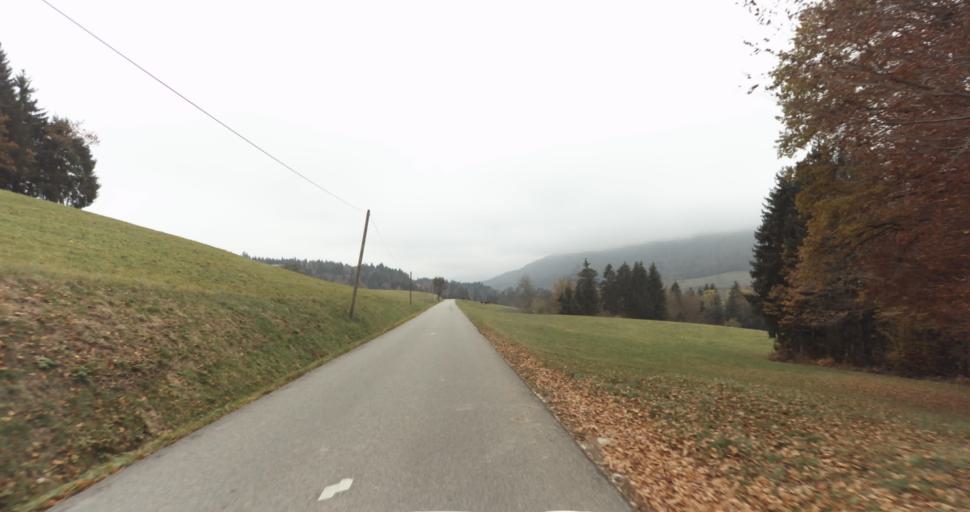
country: FR
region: Rhone-Alpes
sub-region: Departement de la Haute-Savoie
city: Saint-Jorioz
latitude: 45.7674
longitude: 6.1327
